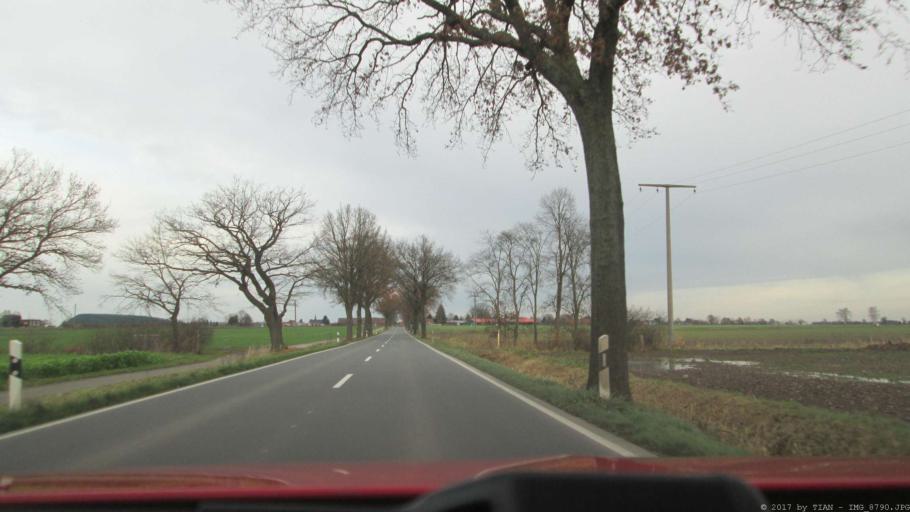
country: DE
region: Lower Saxony
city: Tiddische
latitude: 52.5086
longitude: 10.8037
